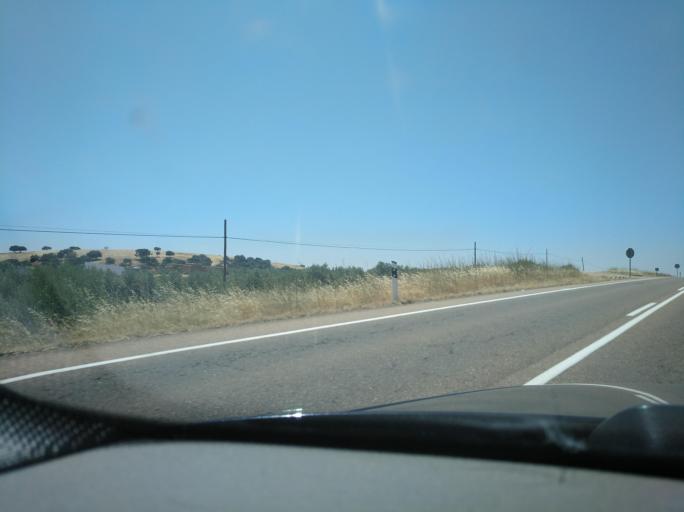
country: ES
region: Extremadura
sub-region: Provincia de Badajoz
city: Olivenza
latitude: 38.7296
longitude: -7.0730
